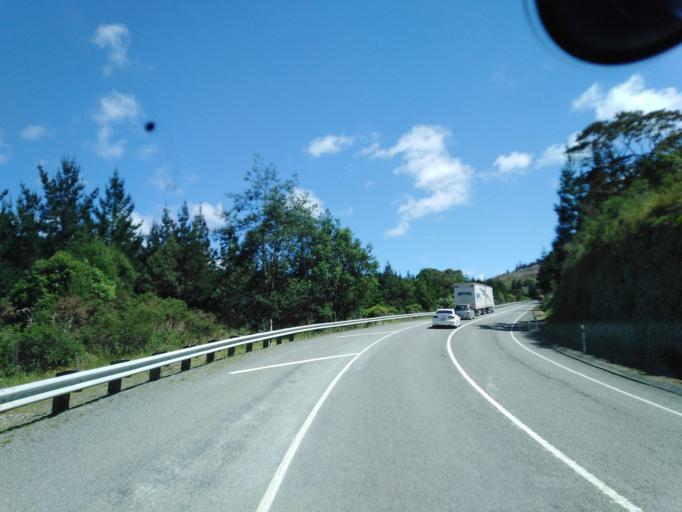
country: NZ
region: Nelson
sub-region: Nelson City
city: Nelson
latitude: -41.1970
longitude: 173.5586
